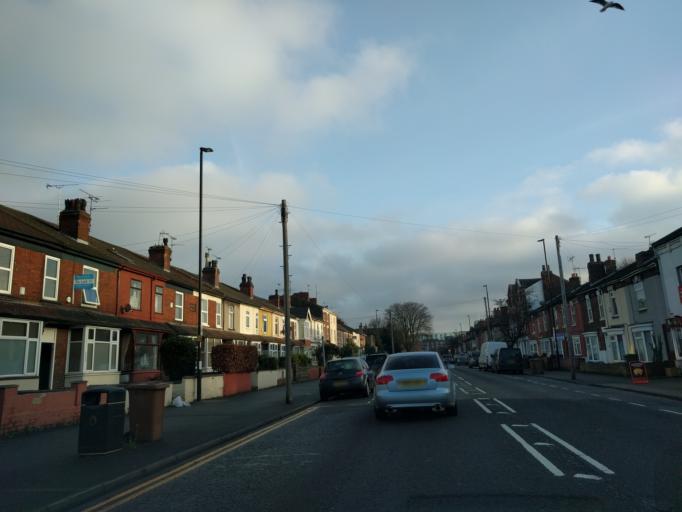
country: GB
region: England
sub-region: Lincolnshire
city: Lincoln
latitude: 53.2326
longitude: -0.5545
